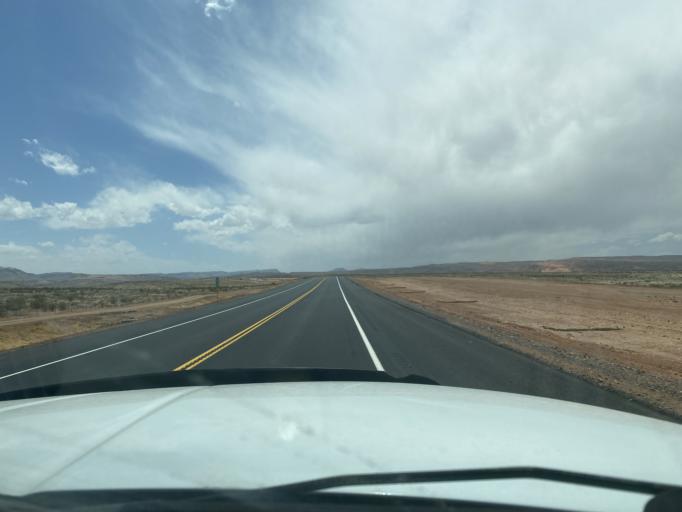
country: US
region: Utah
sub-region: Washington County
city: Hurricane
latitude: 37.1434
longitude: -113.3466
